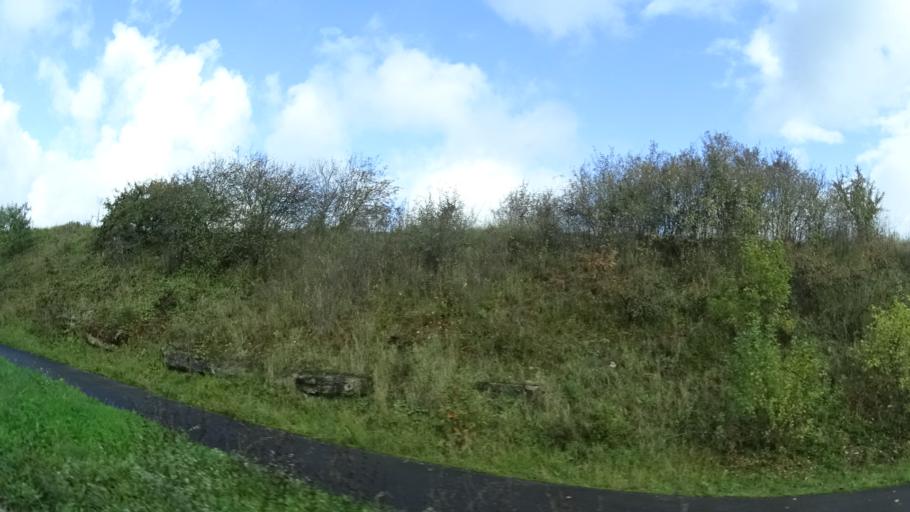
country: DE
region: Bavaria
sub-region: Upper Franconia
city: Burgwindheim
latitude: 49.8798
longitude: 10.5968
